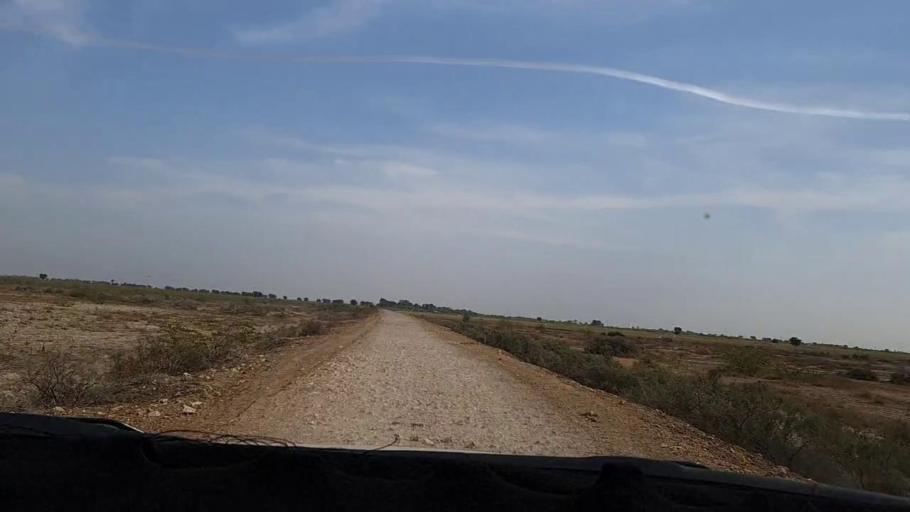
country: PK
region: Sindh
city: Pithoro
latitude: 25.5408
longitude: 69.3338
